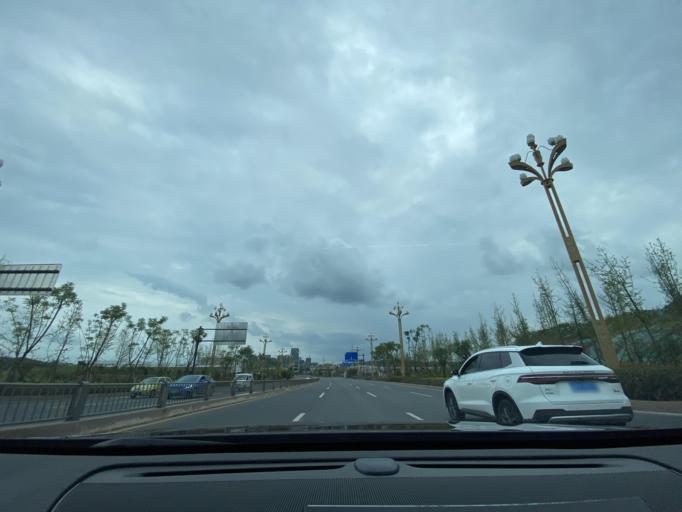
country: CN
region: Sichuan
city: Jiancheng
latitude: 30.4457
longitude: 104.4960
